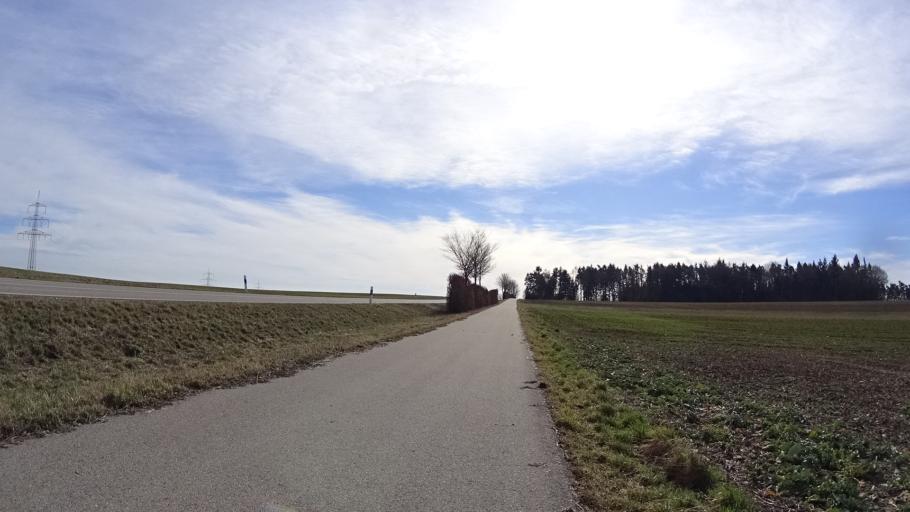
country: DE
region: Bavaria
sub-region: Upper Bavaria
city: Bohmfeld
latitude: 48.8504
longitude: 11.3732
